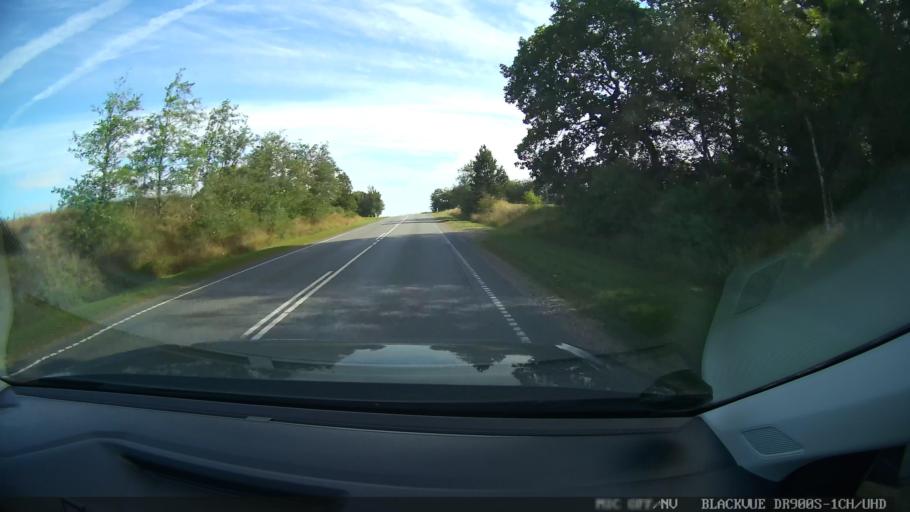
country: DK
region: North Denmark
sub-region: Mariagerfjord Kommune
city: Hadsund
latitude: 56.7966
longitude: 10.0354
